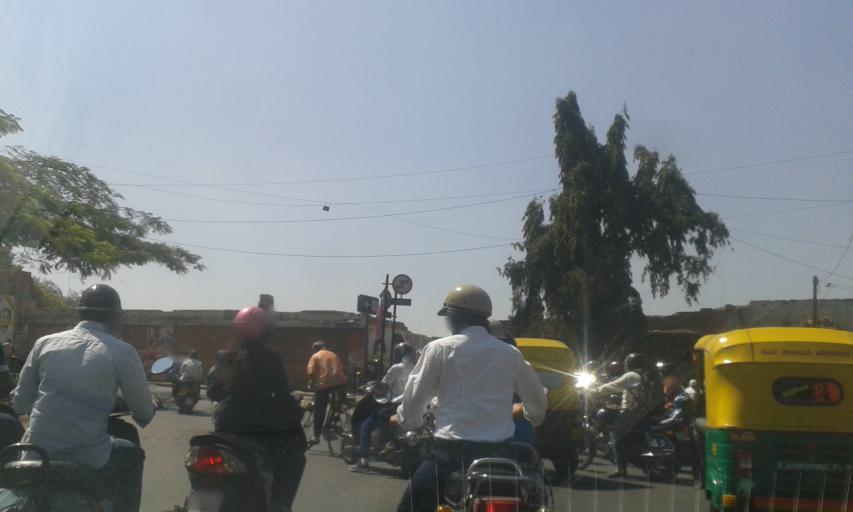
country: IN
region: Karnataka
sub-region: Bangalore Urban
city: Bangalore
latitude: 12.9708
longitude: 77.5666
